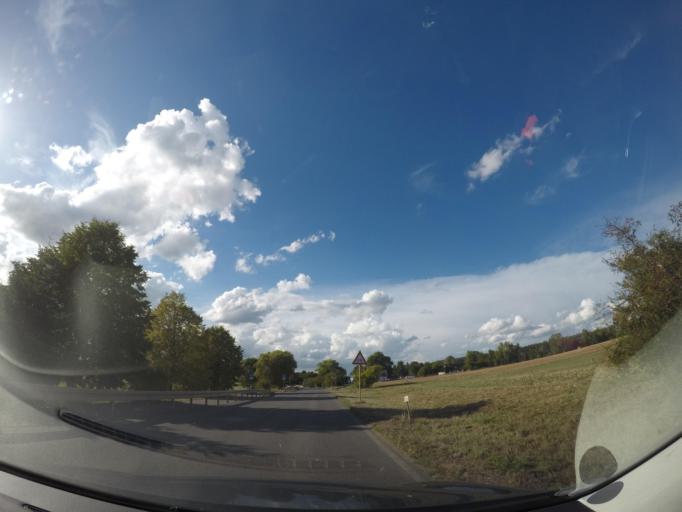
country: DE
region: Saxony-Anhalt
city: Haldensleben I
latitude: 52.3003
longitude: 11.4098
